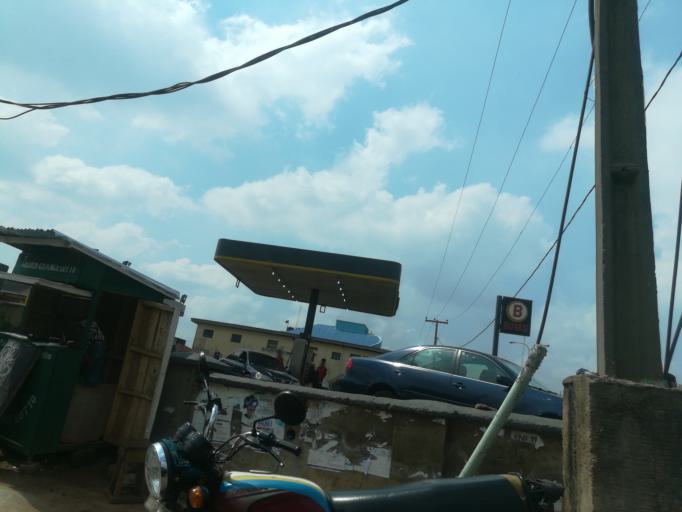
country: NG
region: Oyo
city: Ibadan
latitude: 7.3932
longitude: 3.9044
